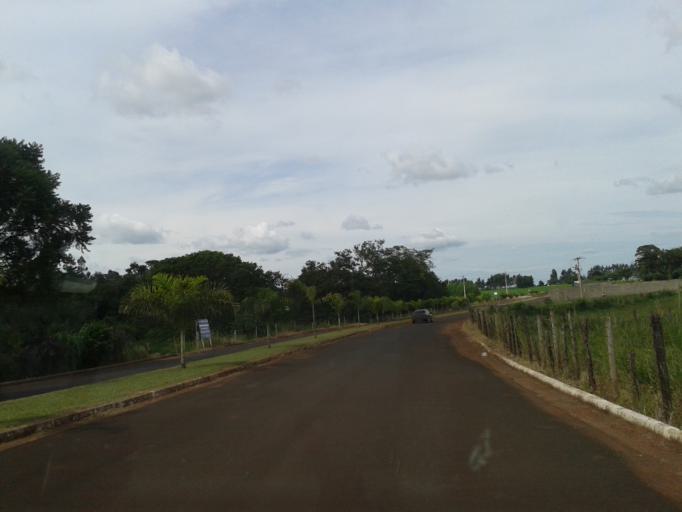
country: BR
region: Minas Gerais
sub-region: Centralina
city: Centralina
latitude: -18.5793
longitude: -49.2015
